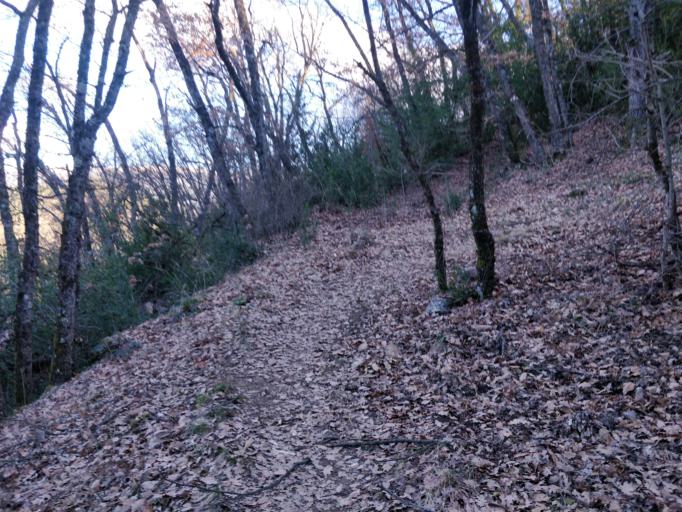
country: FR
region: Provence-Alpes-Cote d'Azur
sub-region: Departement des Alpes-de-Haute-Provence
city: Digne-les-Bains
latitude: 44.1013
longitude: 6.2449
